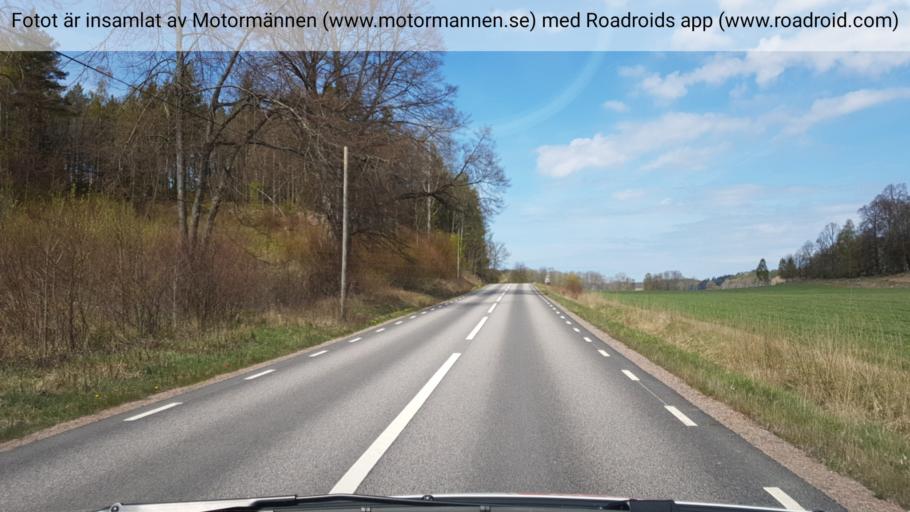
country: SE
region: Kalmar
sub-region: Vasterviks Kommun
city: Forserum
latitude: 57.9177
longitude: 16.6230
